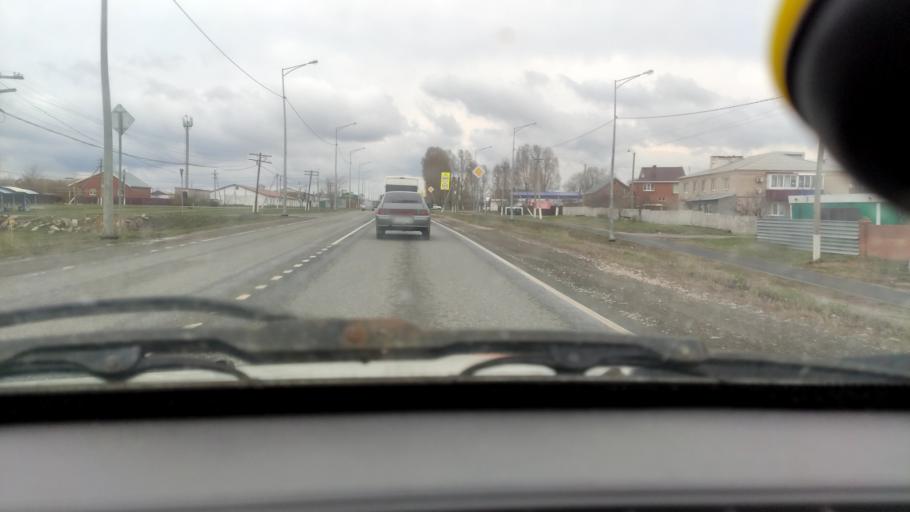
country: RU
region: Samara
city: Zhigulevsk
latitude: 53.5482
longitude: 49.5221
